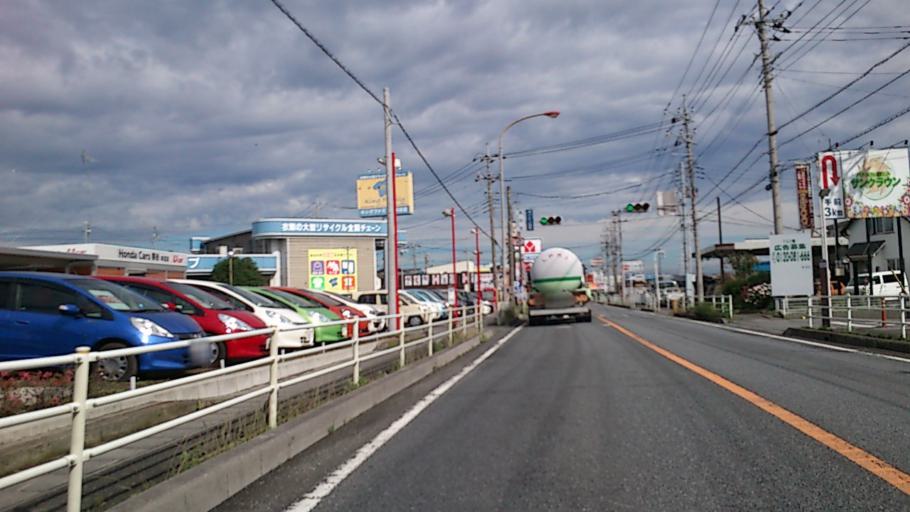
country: JP
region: Saitama
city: Honjo
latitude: 36.2390
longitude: 139.2045
